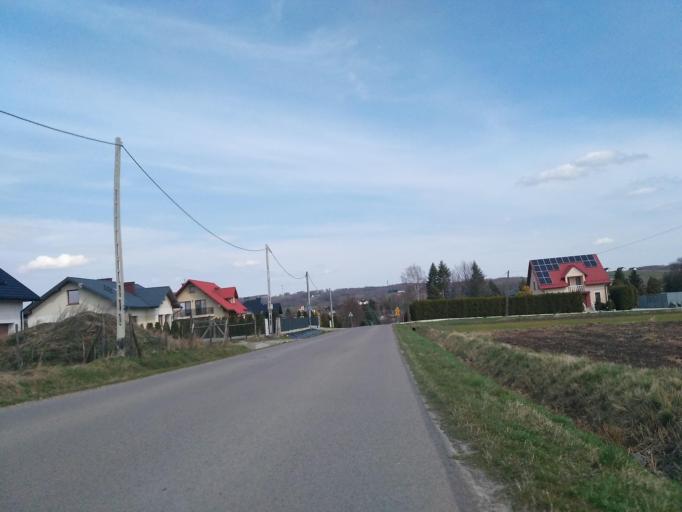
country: PL
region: Subcarpathian Voivodeship
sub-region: Powiat ropczycko-sedziszowski
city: Iwierzyce
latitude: 50.0164
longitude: 21.7848
